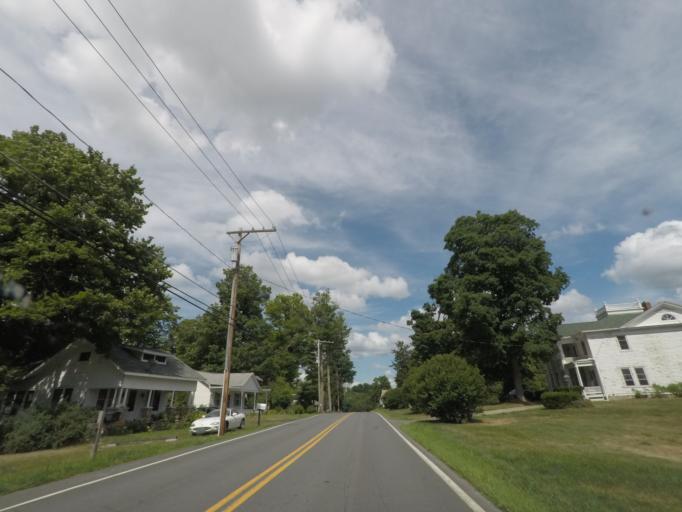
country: US
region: New York
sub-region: Rensselaer County
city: Wynantskill
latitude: 42.7279
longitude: -73.6065
